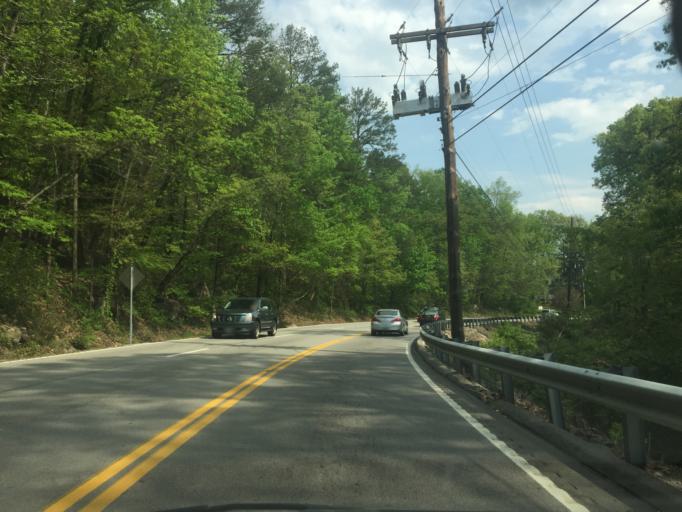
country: US
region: Tennessee
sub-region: Hamilton County
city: Signal Mountain
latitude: 35.1083
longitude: -85.3492
